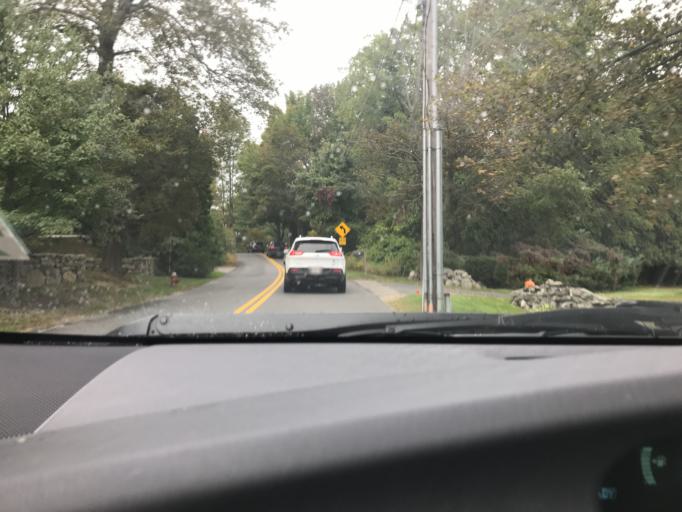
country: US
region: Massachusetts
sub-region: Middlesex County
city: Concord
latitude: 42.4731
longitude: -71.3554
